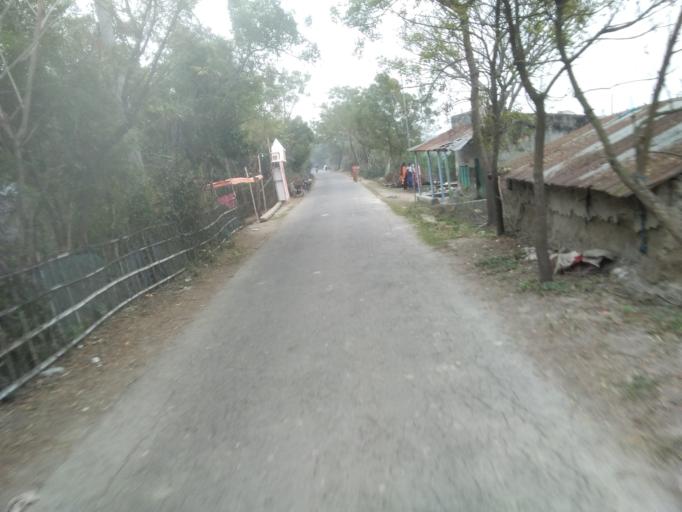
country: BD
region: Khulna
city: Satkhira
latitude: 22.5755
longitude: 89.0750
